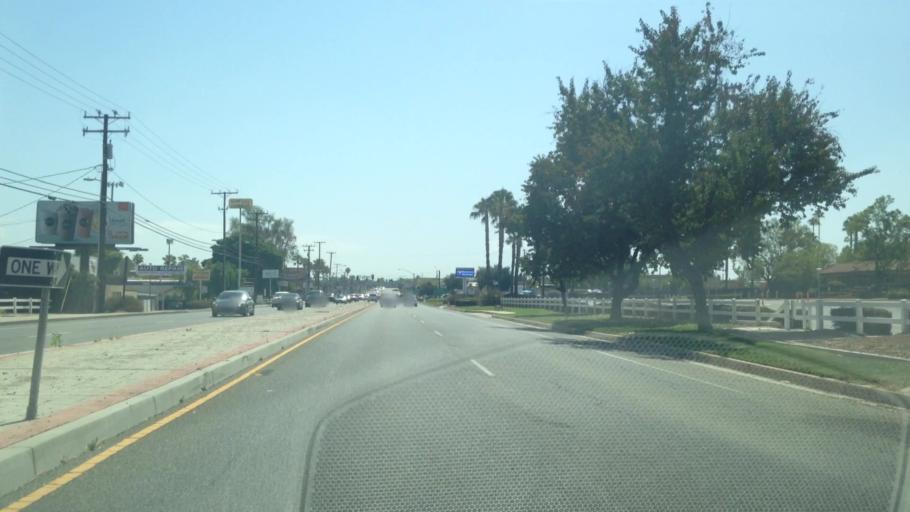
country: US
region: California
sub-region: Riverside County
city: Woodcrest
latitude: 33.8871
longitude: -117.3434
